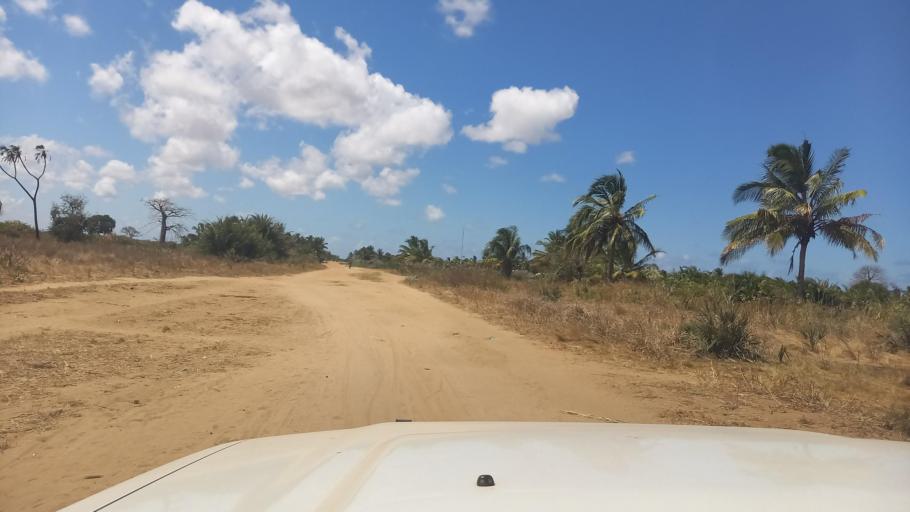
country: MZ
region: Cabo Delgado
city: Pemba
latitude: -13.4222
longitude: 40.5181
